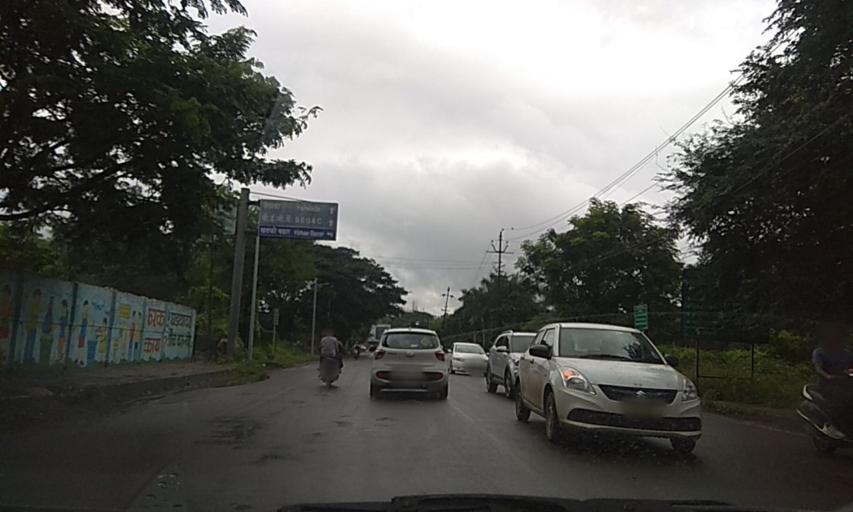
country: IN
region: Maharashtra
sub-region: Pune Division
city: Khadki
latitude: 18.5512
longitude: 73.8559
